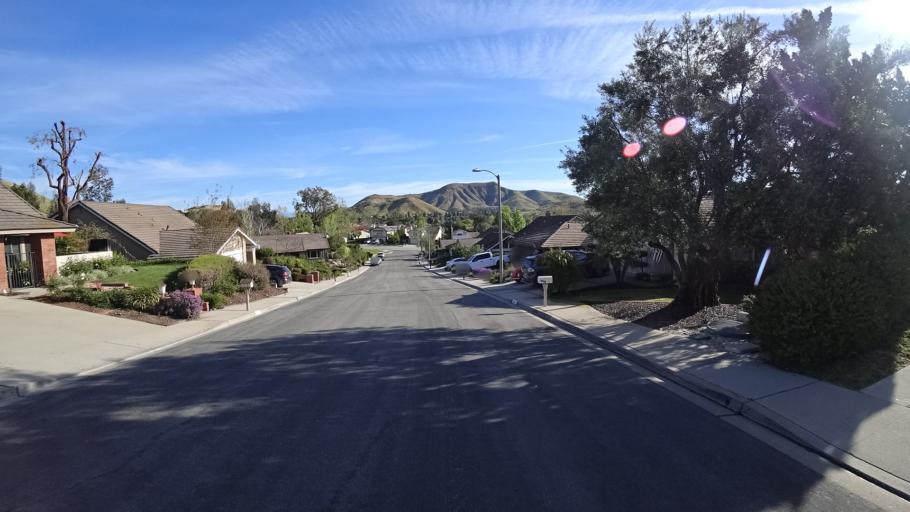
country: US
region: California
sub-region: Ventura County
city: Casa Conejo
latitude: 34.1850
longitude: -118.9577
